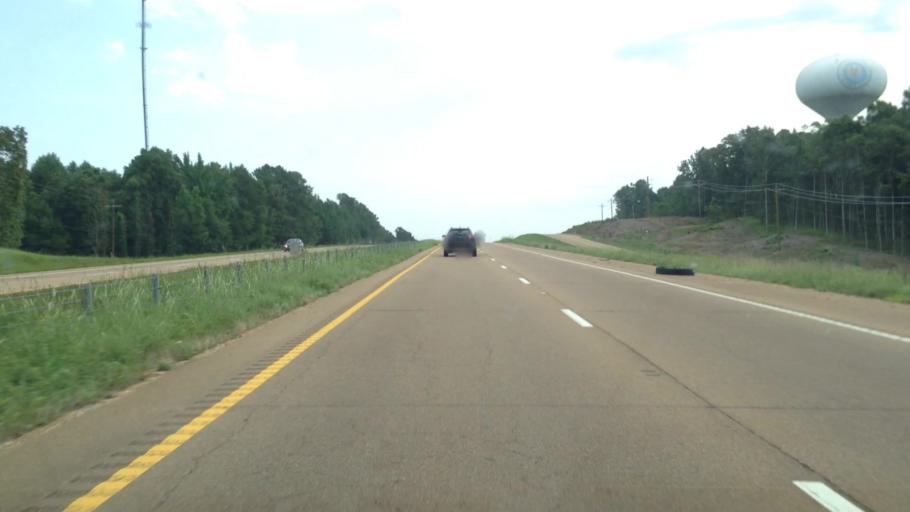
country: US
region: Mississippi
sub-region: Hinds County
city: Byram
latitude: 32.1554
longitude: -90.2750
